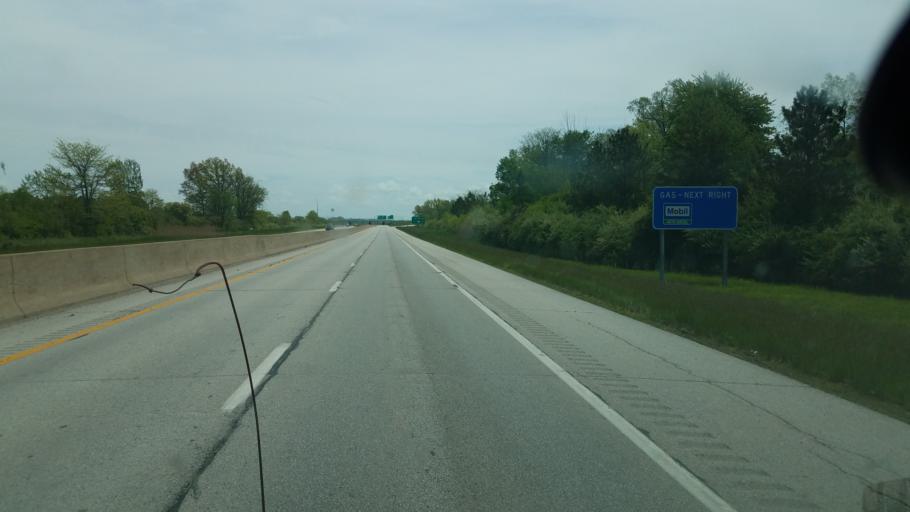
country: US
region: Ohio
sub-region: Ottawa County
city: Port Clinton
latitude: 41.5047
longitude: -82.9789
